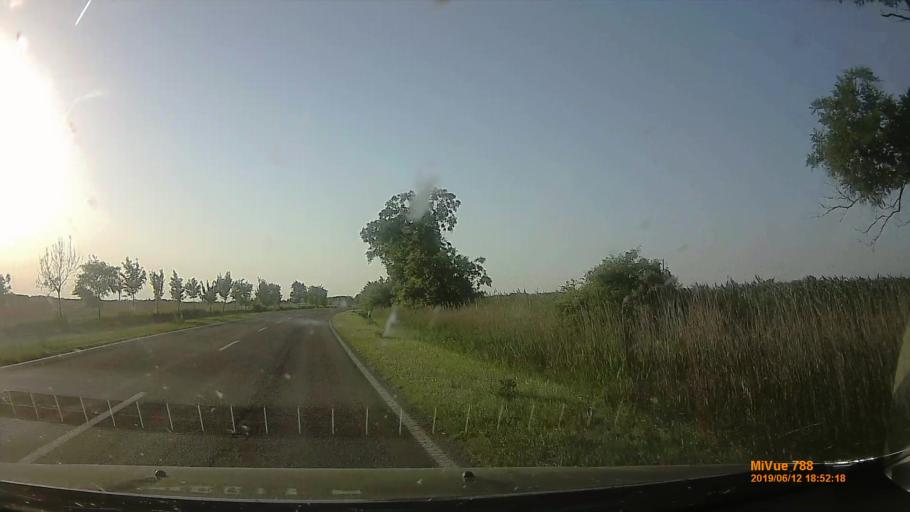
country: HU
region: Bacs-Kiskun
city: Kiskunfelegyhaza
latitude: 46.6729
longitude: 19.8558
